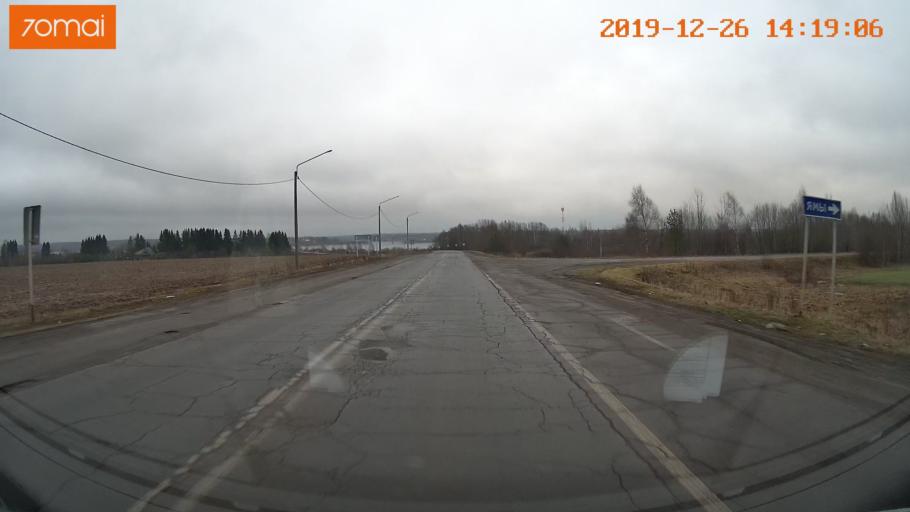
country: RU
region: Jaroslavl
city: Poshekhon'ye
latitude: 58.5118
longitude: 39.1088
